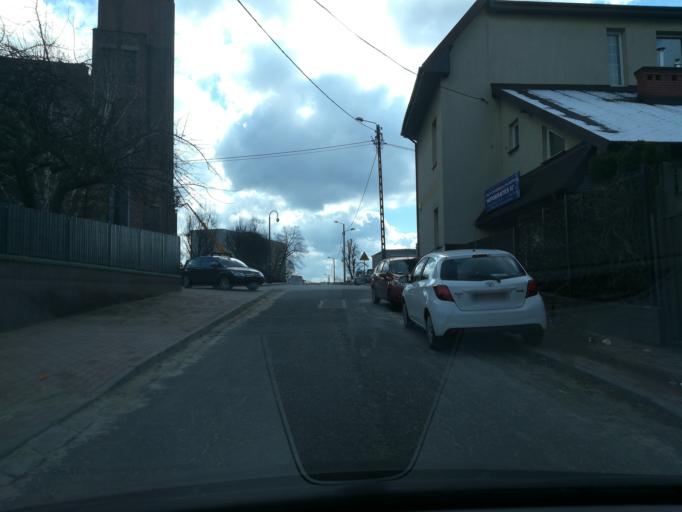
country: PL
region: Silesian Voivodeship
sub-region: Czestochowa
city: Czestochowa
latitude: 50.7930
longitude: 19.1327
